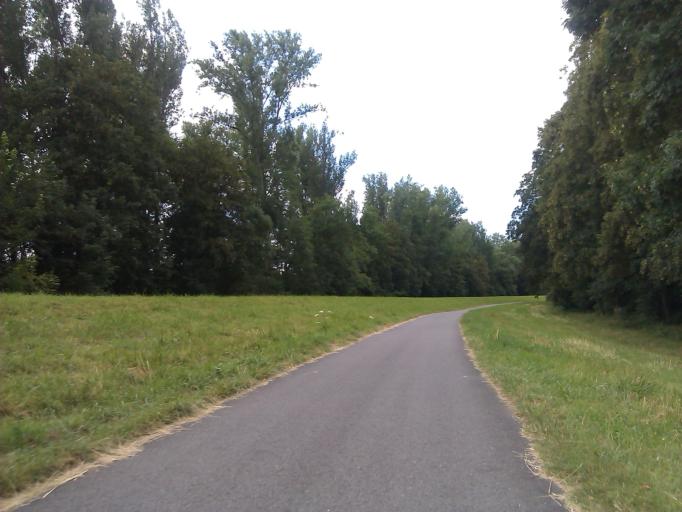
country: DE
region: Rheinland-Pfalz
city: Altrip
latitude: 49.3987
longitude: 8.4813
